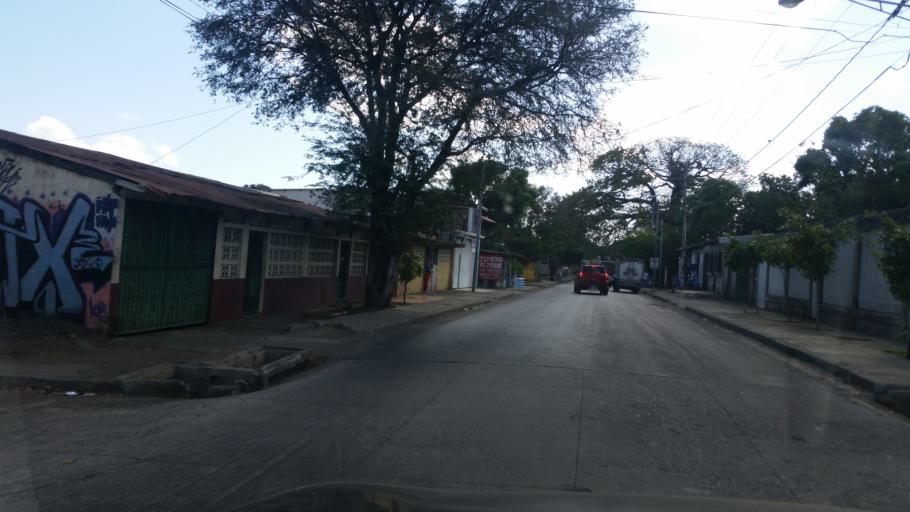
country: NI
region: Managua
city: Managua
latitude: 12.1371
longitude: -86.2346
